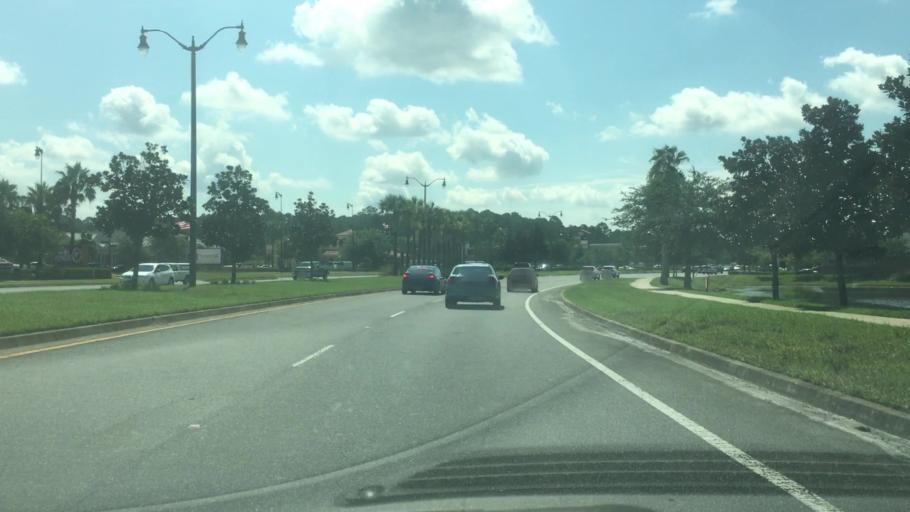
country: US
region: Florida
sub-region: Duval County
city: Jacksonville
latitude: 30.4810
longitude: -81.6380
